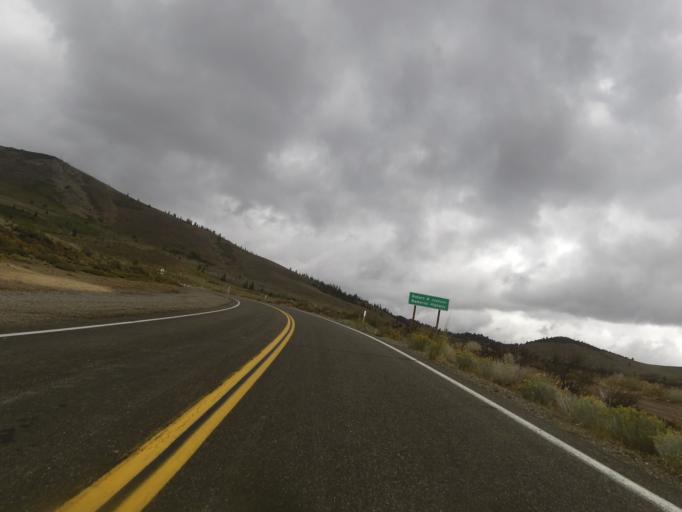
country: US
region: Nevada
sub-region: Douglas County
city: Gardnerville Ranchos
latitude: 38.6805
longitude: -119.5926
